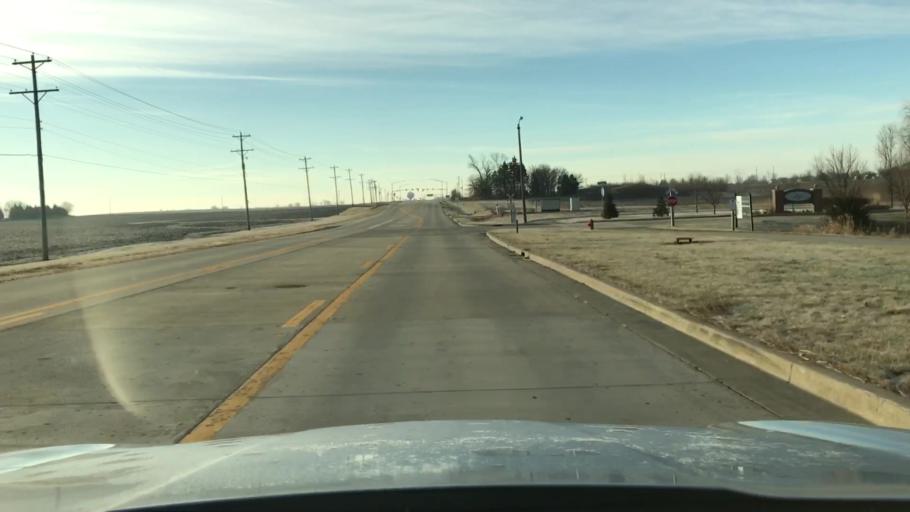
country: US
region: Illinois
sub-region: McLean County
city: Normal
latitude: 40.5520
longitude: -88.9444
